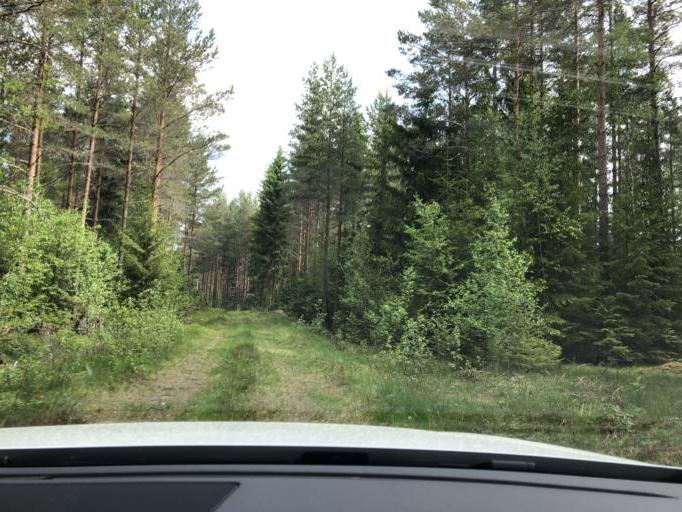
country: SE
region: Dalarna
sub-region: Avesta Kommun
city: Horndal
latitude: 60.2186
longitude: 16.5049
